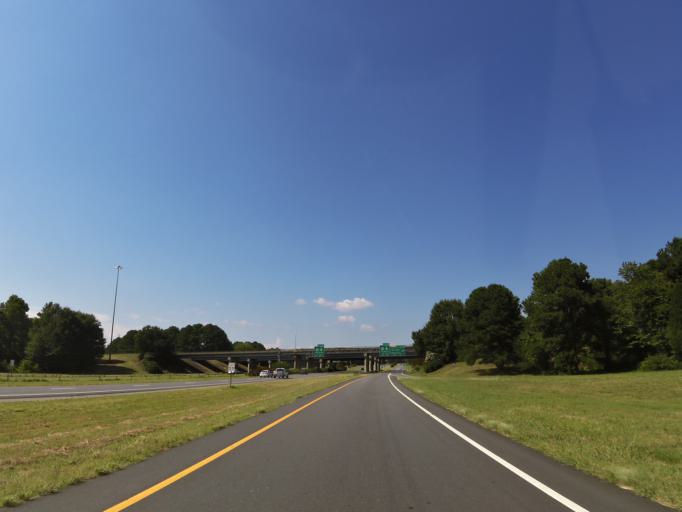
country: US
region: North Carolina
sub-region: Catawba County
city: Mountain View
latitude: 35.7062
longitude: -81.3523
